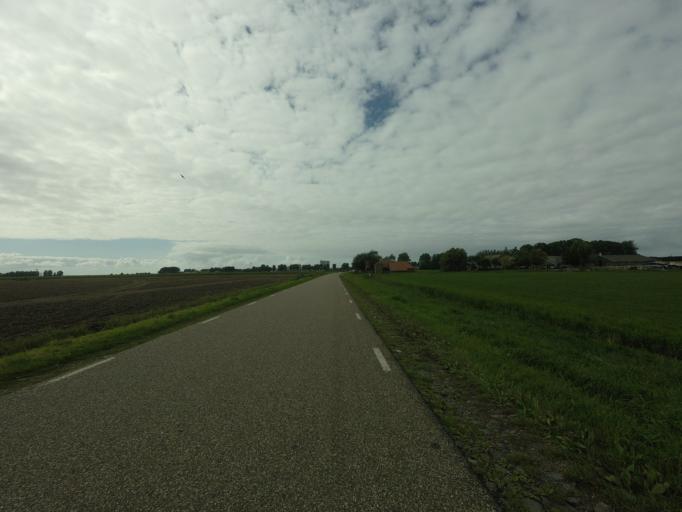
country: NL
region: Friesland
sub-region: Sudwest Fryslan
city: Workum
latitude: 52.9714
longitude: 5.4678
